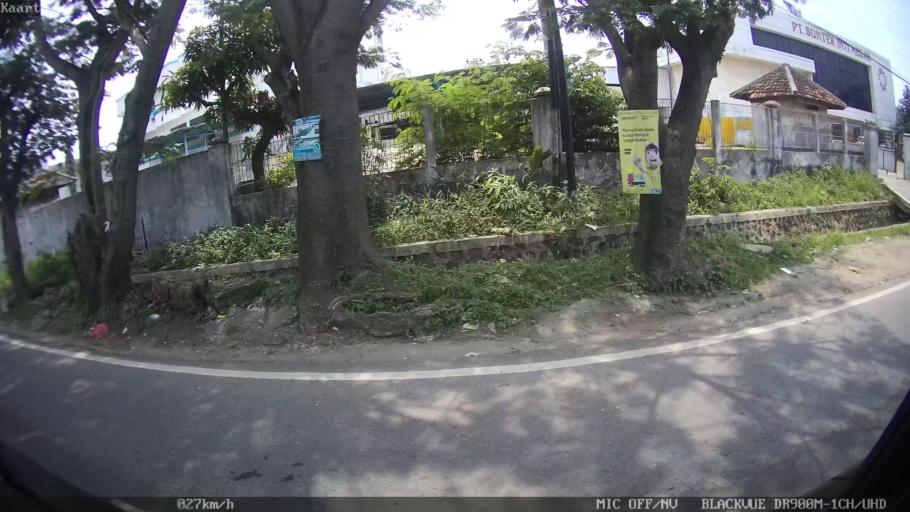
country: ID
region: Lampung
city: Kedaton
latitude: -5.3537
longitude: 105.2195
